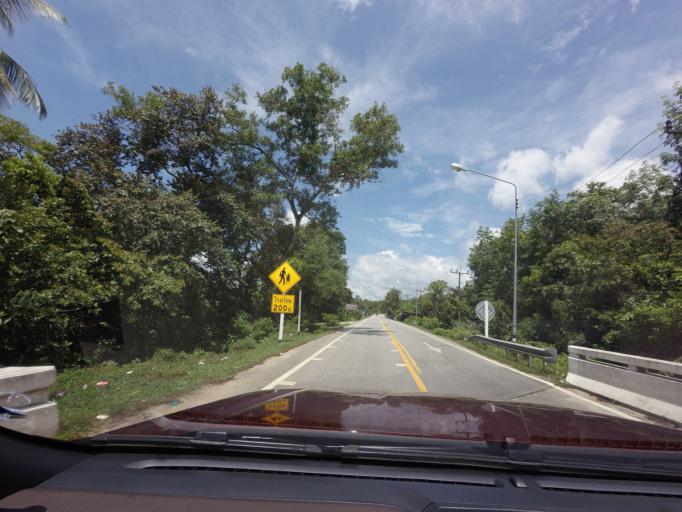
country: TH
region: Narathiwat
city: Ra-ngae
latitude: 6.2649
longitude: 101.6941
